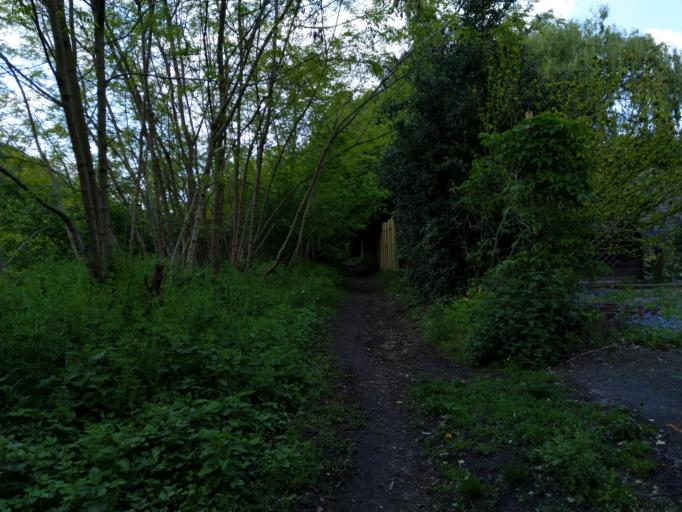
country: BE
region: Wallonia
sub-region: Province du Hainaut
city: Mons
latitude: 50.4805
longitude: 3.9383
